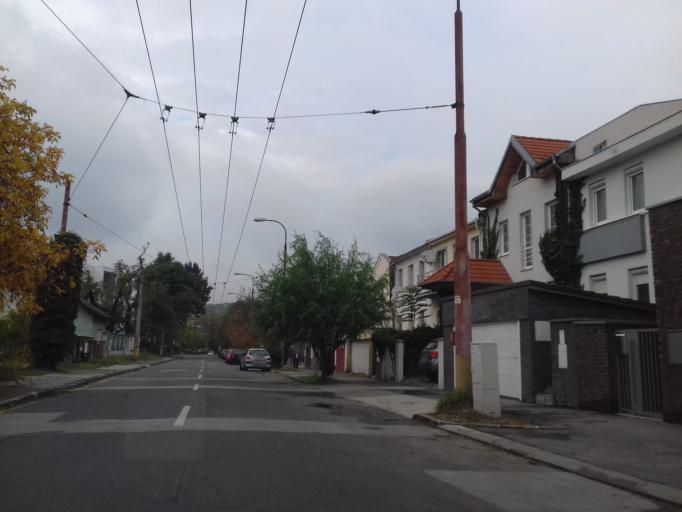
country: SK
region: Bratislavsky
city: Bratislava
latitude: 48.1692
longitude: 17.0781
